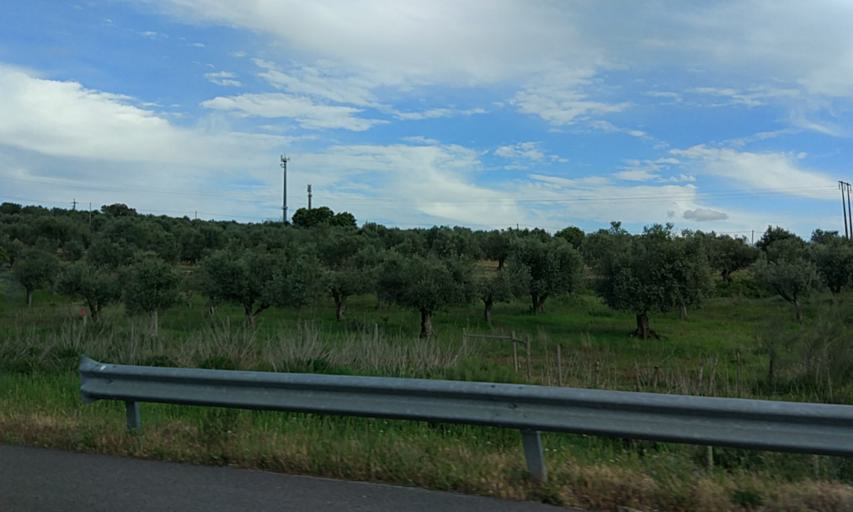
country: PT
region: Portalegre
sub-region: Elvas
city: Elvas
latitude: 38.8754
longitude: -7.2676
